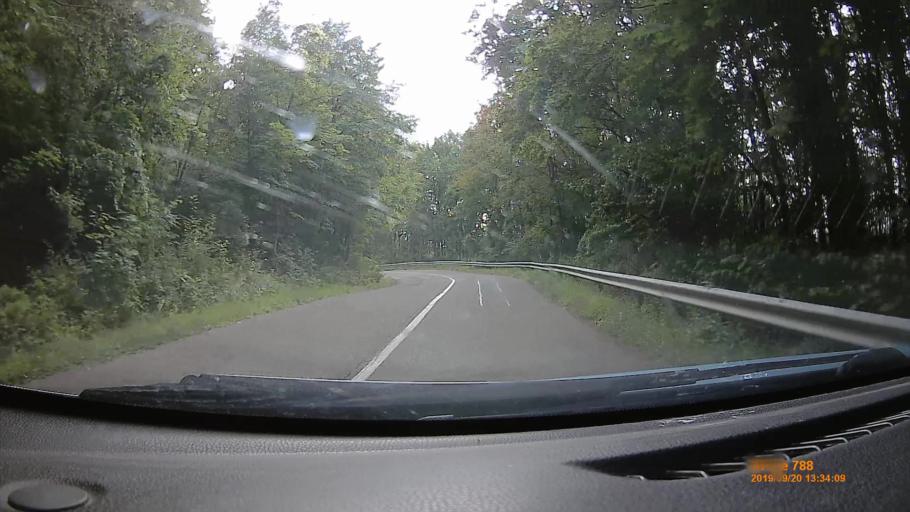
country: HU
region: Heves
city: Szilvasvarad
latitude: 48.0579
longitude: 20.5059
